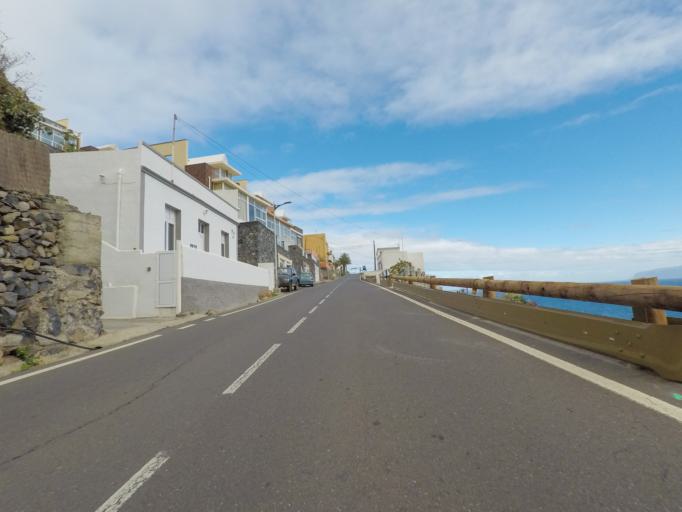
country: ES
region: Canary Islands
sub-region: Provincia de Santa Cruz de Tenerife
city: Hermigua
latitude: 28.1778
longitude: -17.1857
